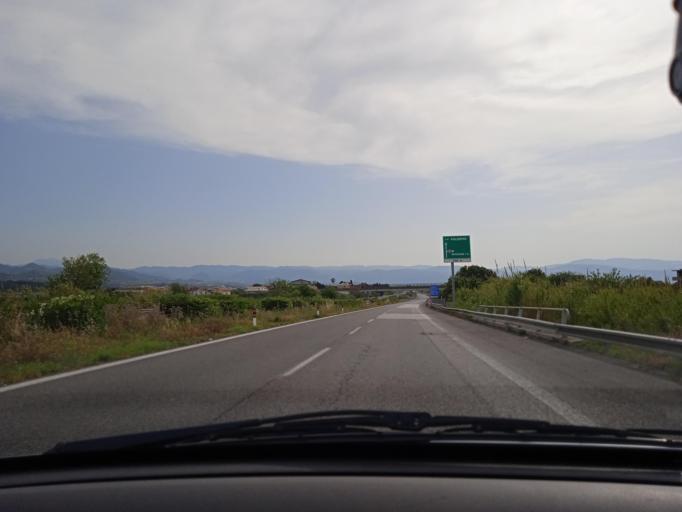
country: IT
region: Sicily
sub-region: Messina
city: Barcellona Pozzo di Gotto
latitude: 38.1615
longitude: 15.1977
